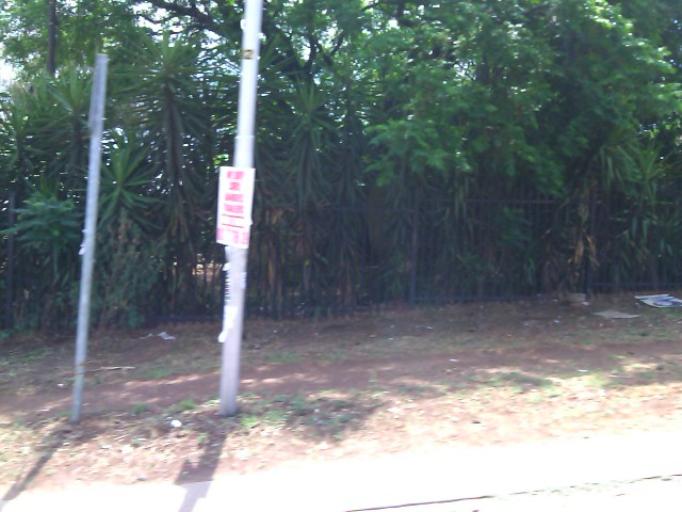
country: ZA
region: Gauteng
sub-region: City of Tshwane Metropolitan Municipality
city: Centurion
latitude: -25.8453
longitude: 28.1928
